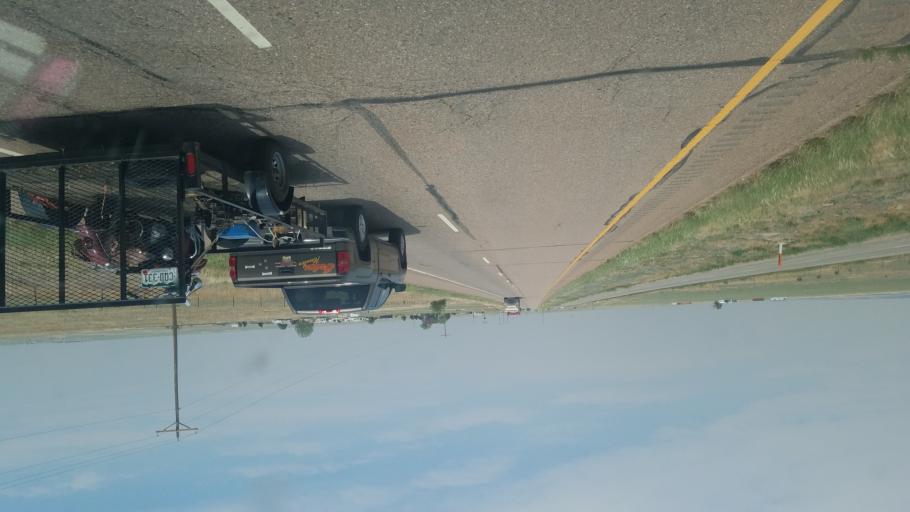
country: US
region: Colorado
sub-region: Fremont County
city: Penrose
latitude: 38.3683
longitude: -104.9199
